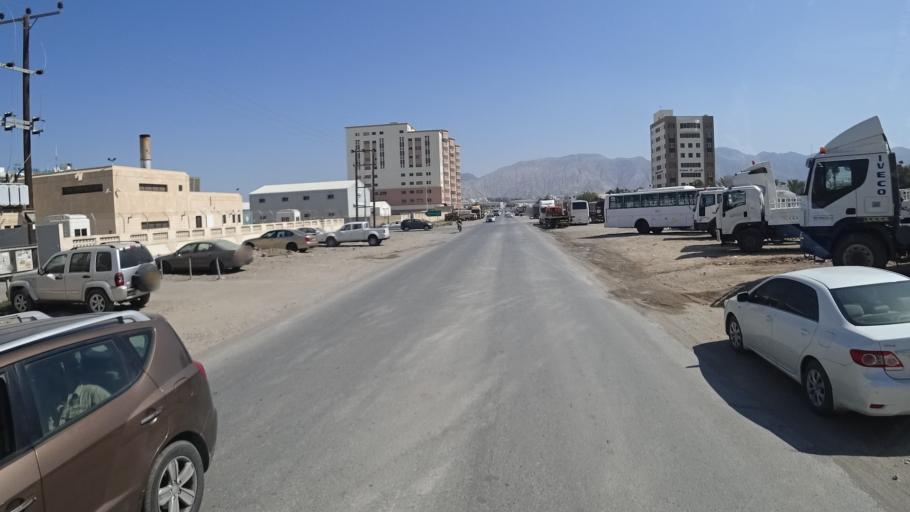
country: OM
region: Muhafazat Masqat
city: Bawshar
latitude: 23.5738
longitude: 58.3738
